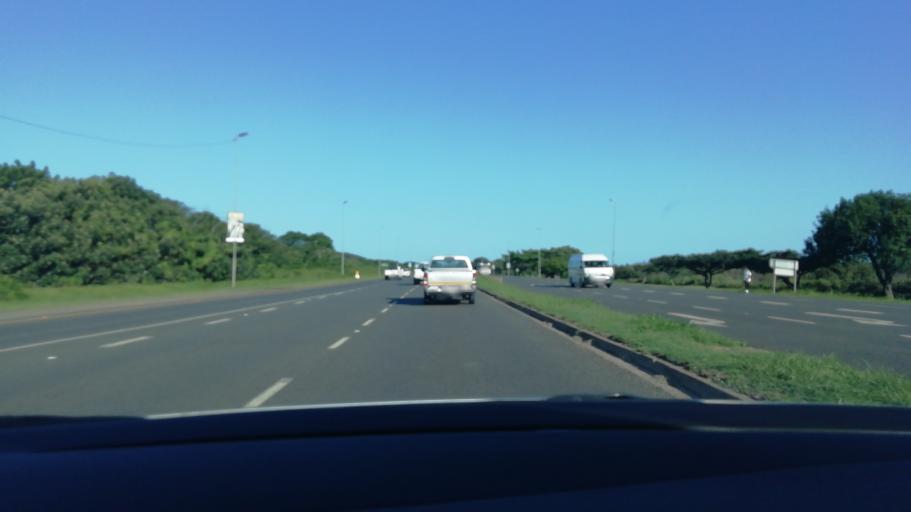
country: ZA
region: KwaZulu-Natal
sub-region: uThungulu District Municipality
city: Richards Bay
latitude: -28.7695
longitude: 32.0600
